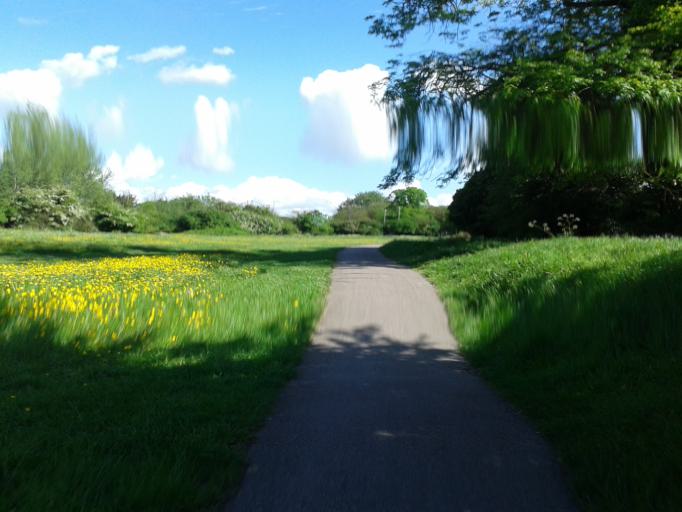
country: GB
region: England
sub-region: Cambridgeshire
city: Cambridge
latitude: 52.2118
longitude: 0.1529
